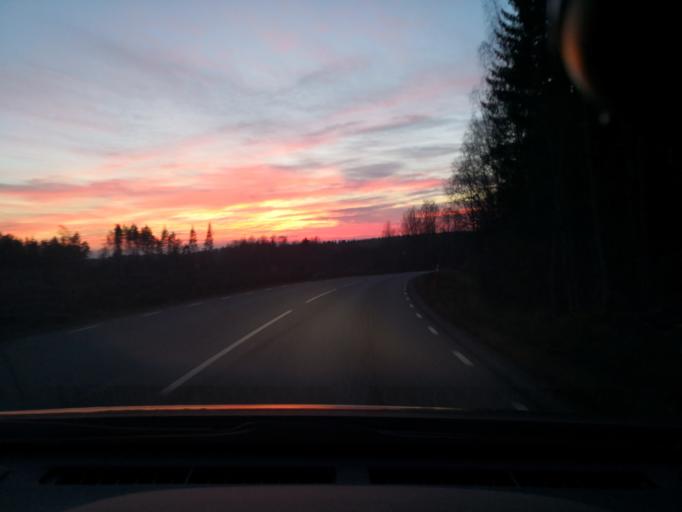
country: SE
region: OErebro
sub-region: Lindesbergs Kommun
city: Frovi
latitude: 59.3752
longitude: 15.4391
